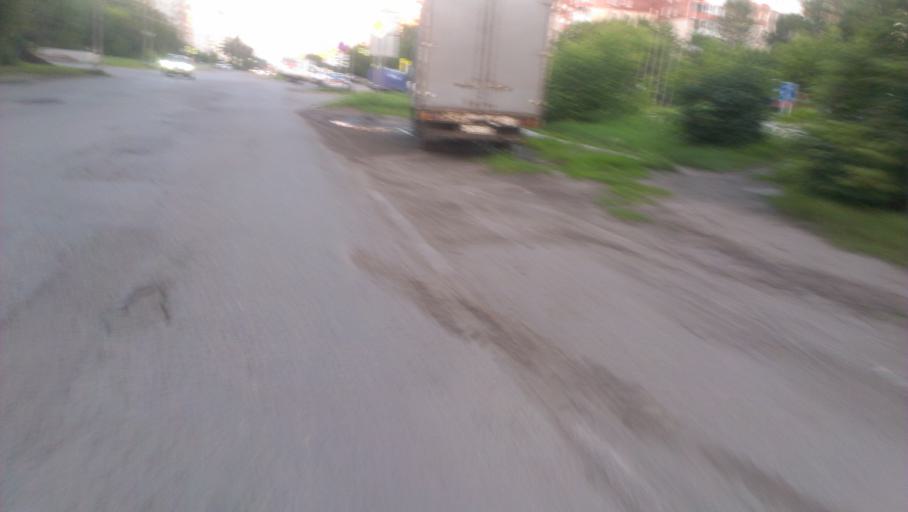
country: RU
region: Altai Krai
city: Novosilikatnyy
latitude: 53.3629
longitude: 83.6663
